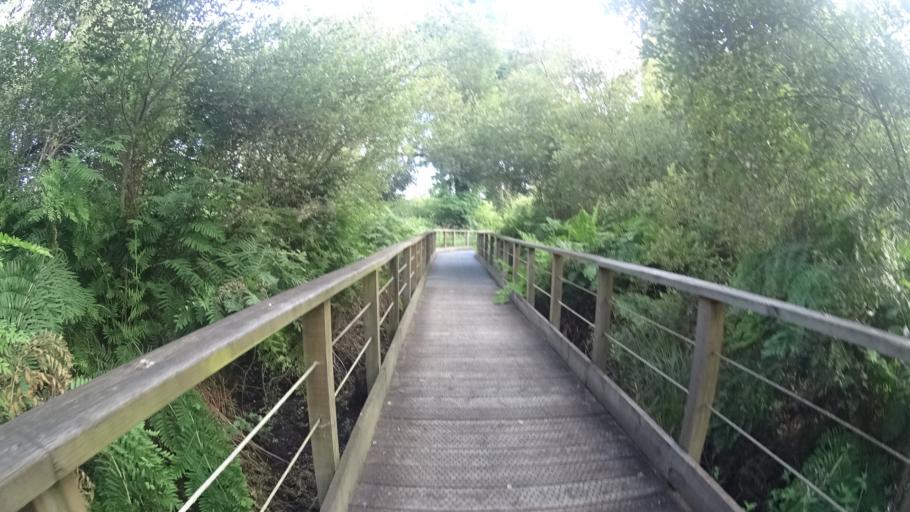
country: FR
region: Aquitaine
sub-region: Departement de la Gironde
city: Hourtin
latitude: 45.2169
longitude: -1.1292
